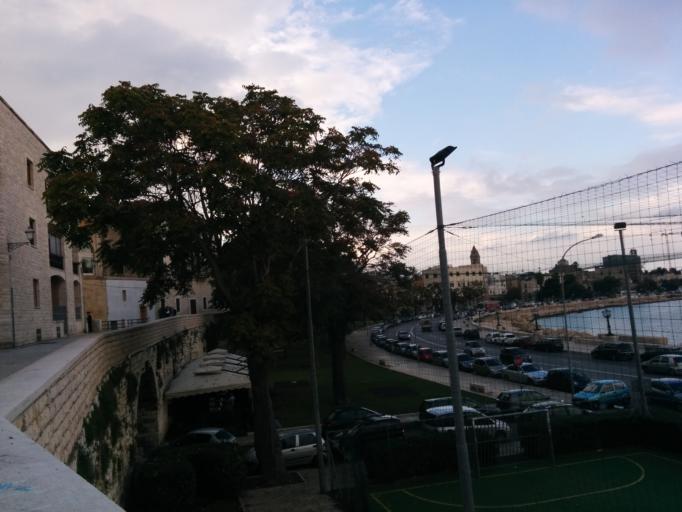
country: IT
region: Apulia
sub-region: Provincia di Bari
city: Bari
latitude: 41.1289
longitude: 16.8725
